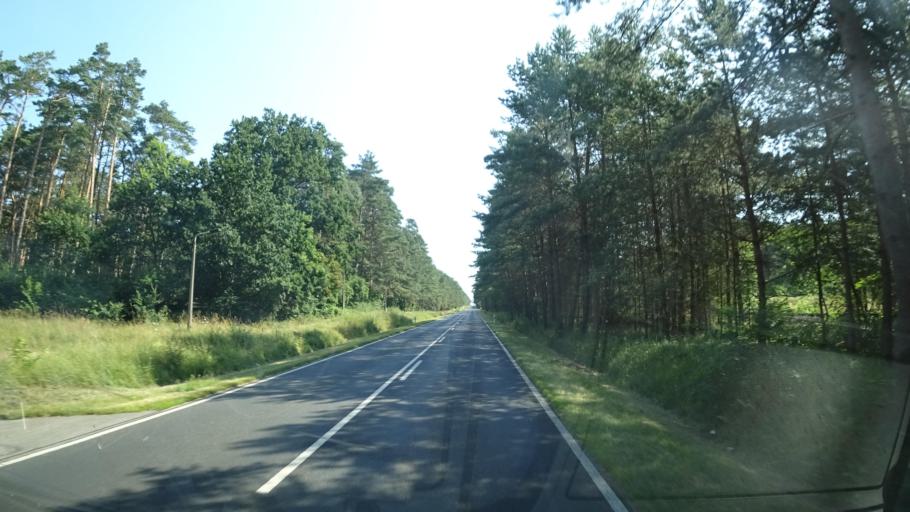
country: DE
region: Mecklenburg-Vorpommern
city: Lubmin
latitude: 54.1323
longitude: 13.6303
